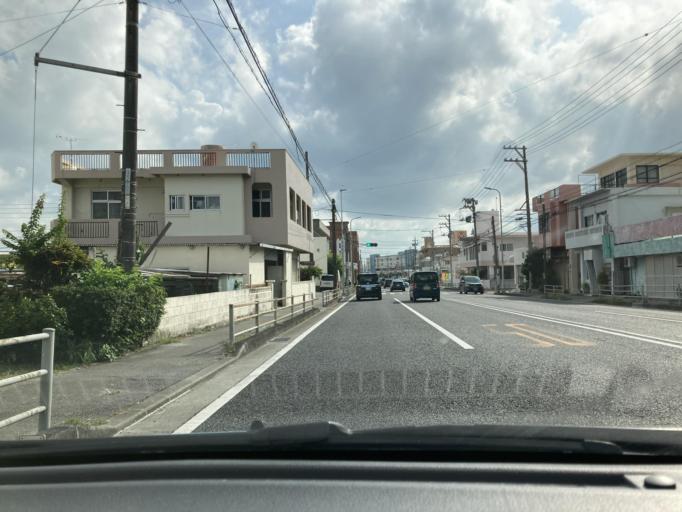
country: JP
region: Okinawa
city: Ginowan
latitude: 26.2280
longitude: 127.7673
